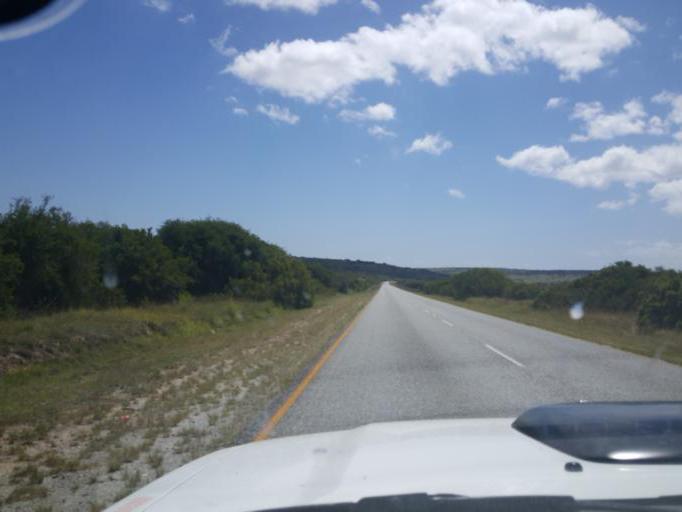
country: ZA
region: Eastern Cape
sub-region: Cacadu District Municipality
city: Grahamstown
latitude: -33.5345
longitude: 26.0744
